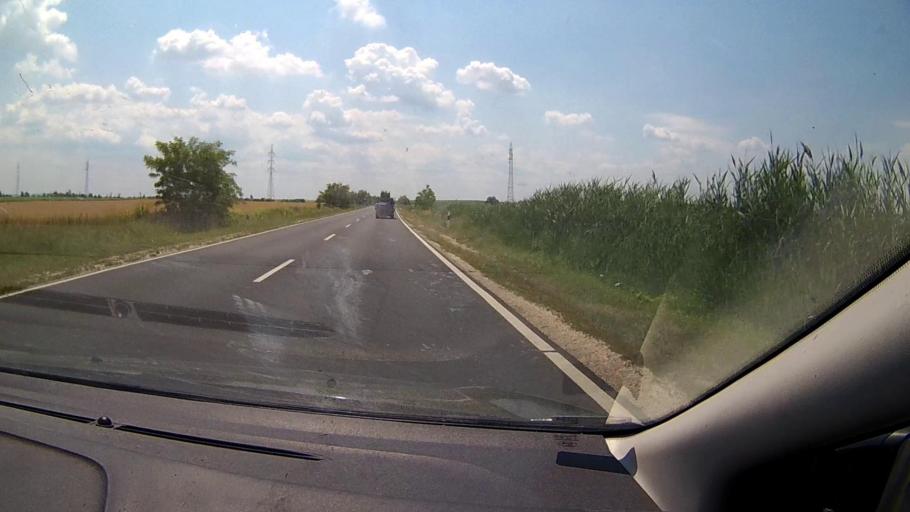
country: HU
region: Komarom-Esztergom
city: Tata
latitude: 47.6139
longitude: 18.3170
